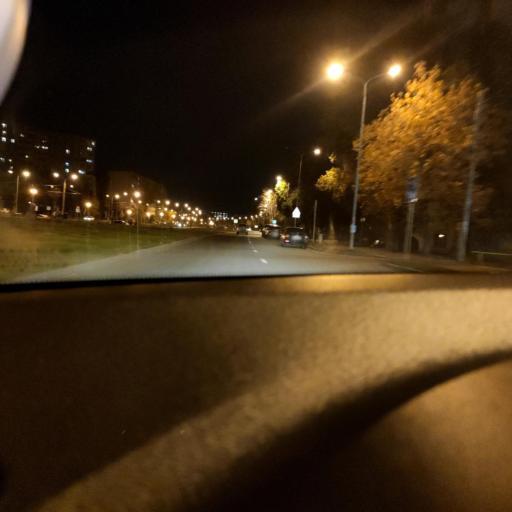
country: RU
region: Samara
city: Samara
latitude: 53.2504
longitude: 50.2473
